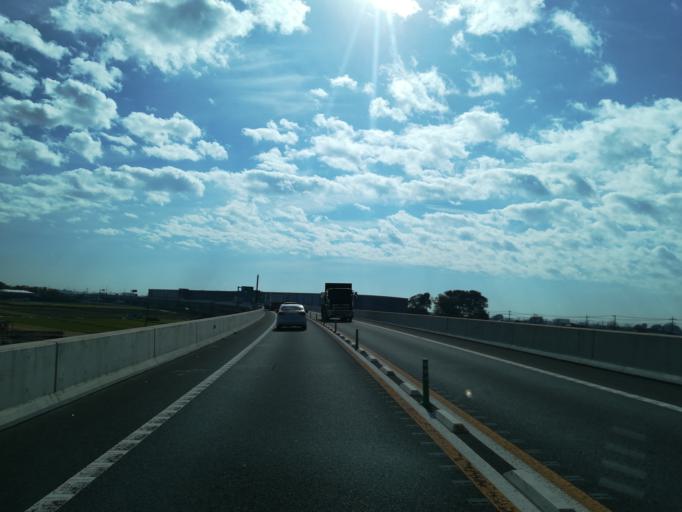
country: JP
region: Ibaraki
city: Sakai
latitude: 36.1044
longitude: 139.7566
